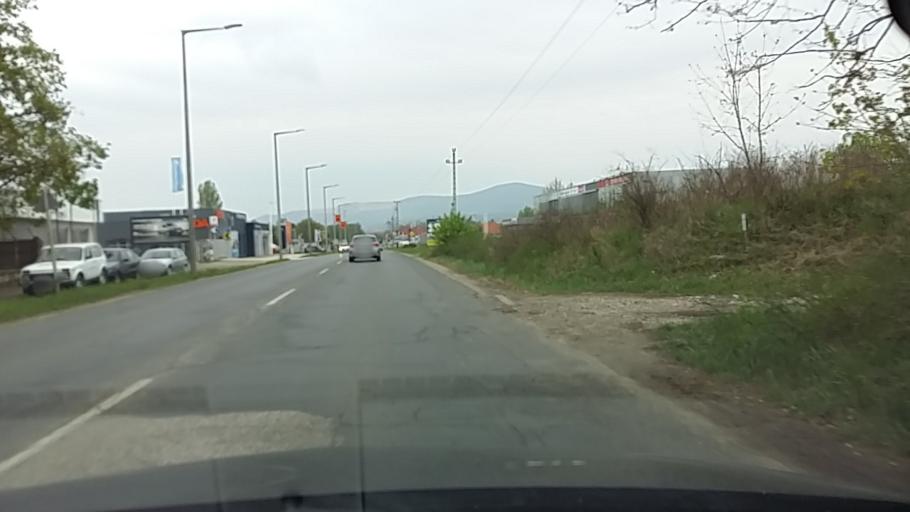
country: HU
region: Pest
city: Vac
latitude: 47.7592
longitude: 19.1410
